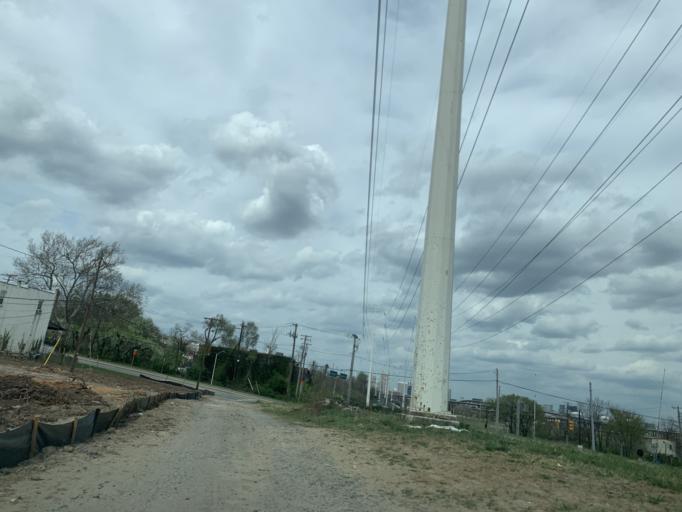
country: US
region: Maryland
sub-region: Baltimore County
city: Baltimore Highlands
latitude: 39.2584
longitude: -76.6346
